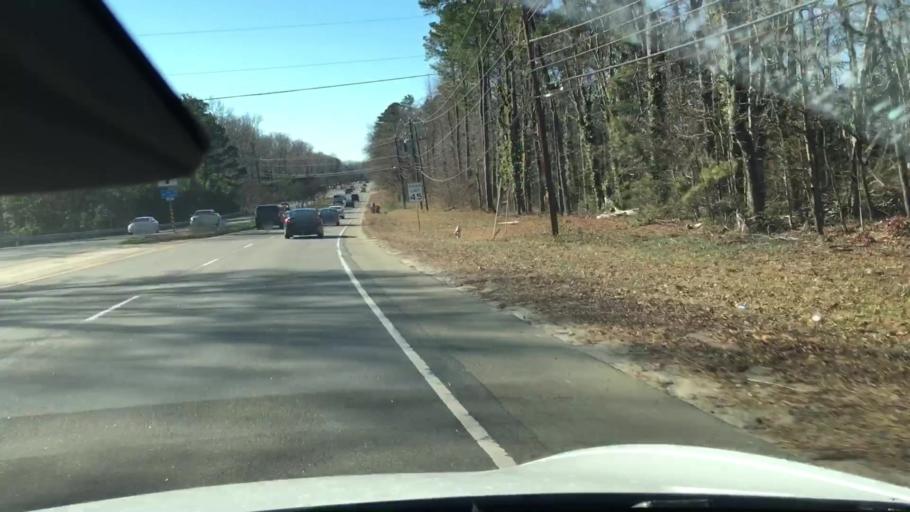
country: US
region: Virginia
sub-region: Chesterfield County
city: Bon Air
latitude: 37.5350
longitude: -77.5674
